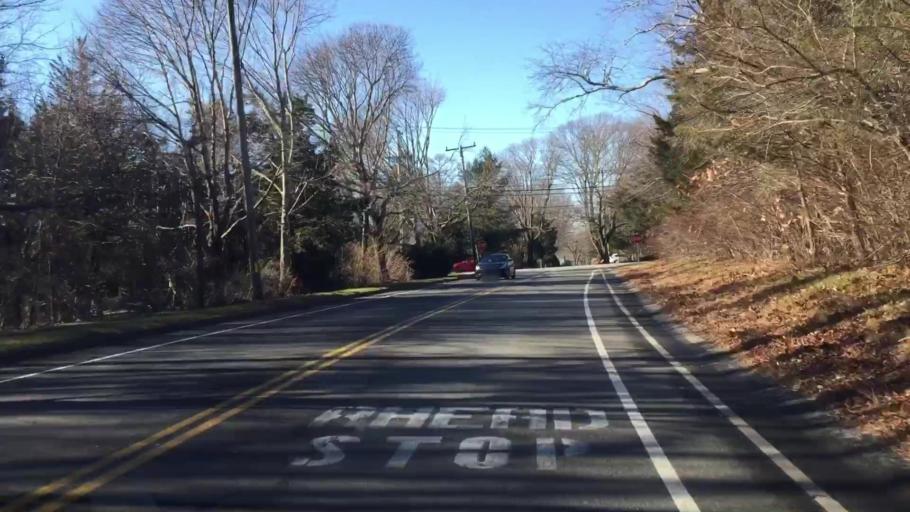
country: US
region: Massachusetts
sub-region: Barnstable County
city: Falmouth
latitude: 41.5552
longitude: -70.6099
